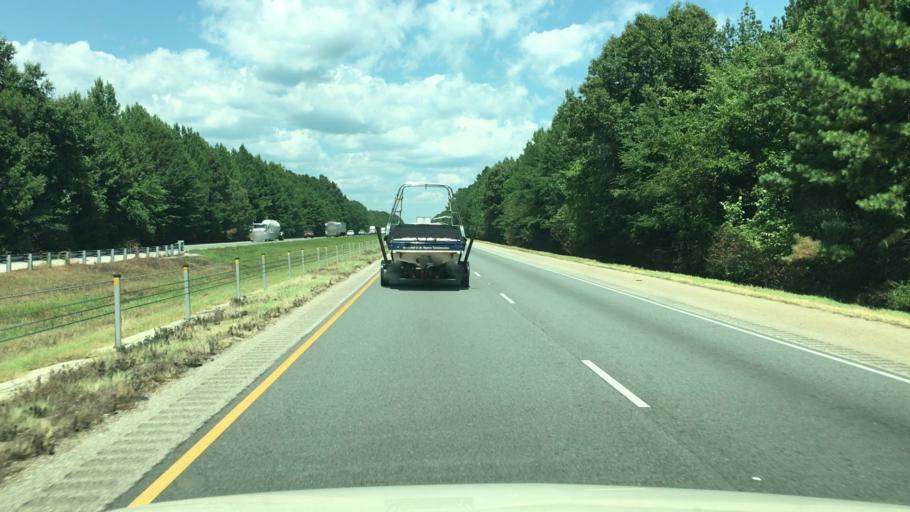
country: US
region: Arkansas
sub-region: Clark County
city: Arkadelphia
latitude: 34.0804
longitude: -93.1155
